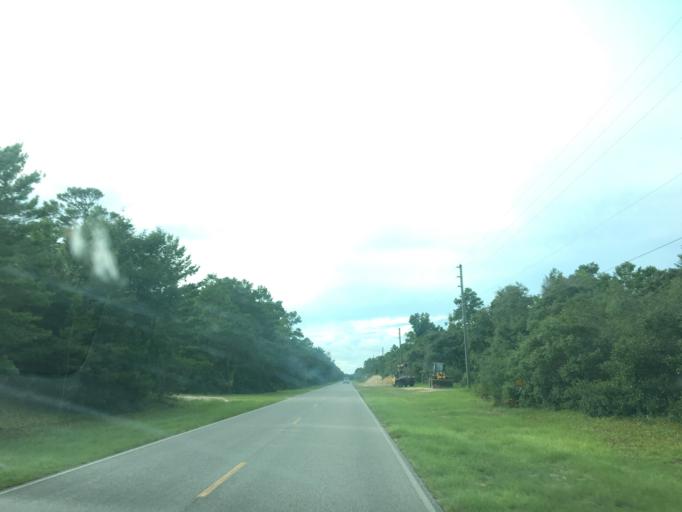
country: US
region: Florida
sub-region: Wakulla County
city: Crawfordville
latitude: 29.9162
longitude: -84.3688
